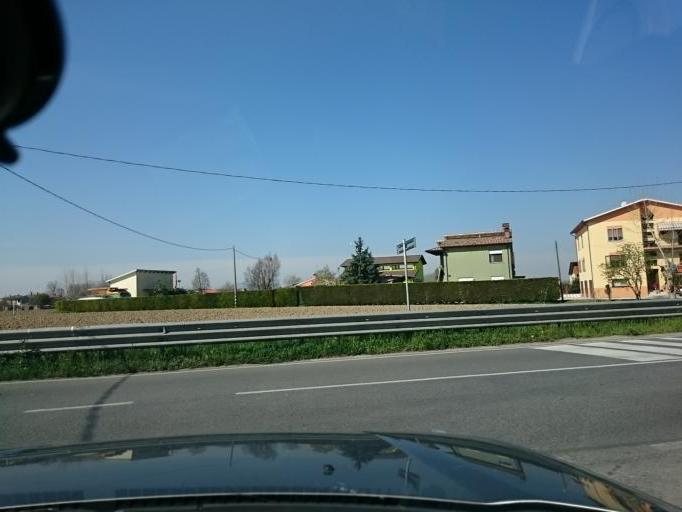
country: IT
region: Veneto
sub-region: Provincia di Padova
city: Albignasego
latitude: 45.3521
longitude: 11.8975
